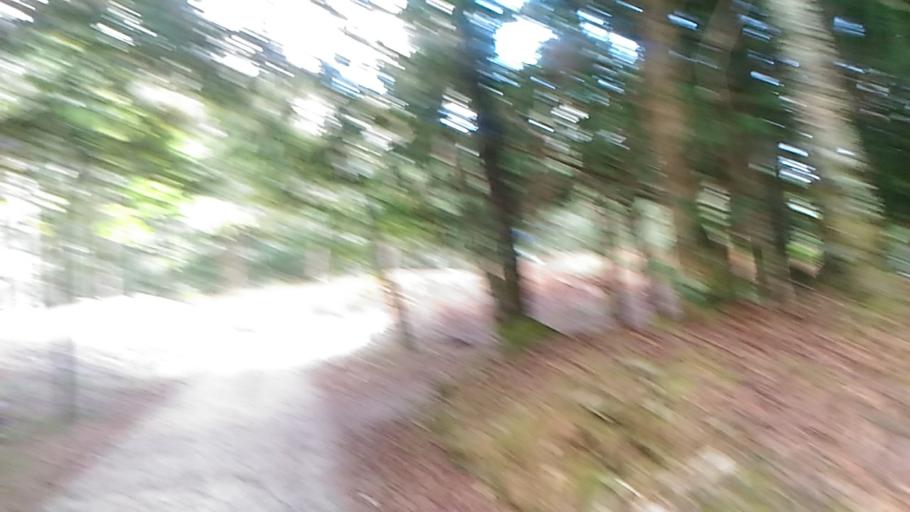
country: TW
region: Taiwan
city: Daxi
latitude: 24.4073
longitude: 121.3051
